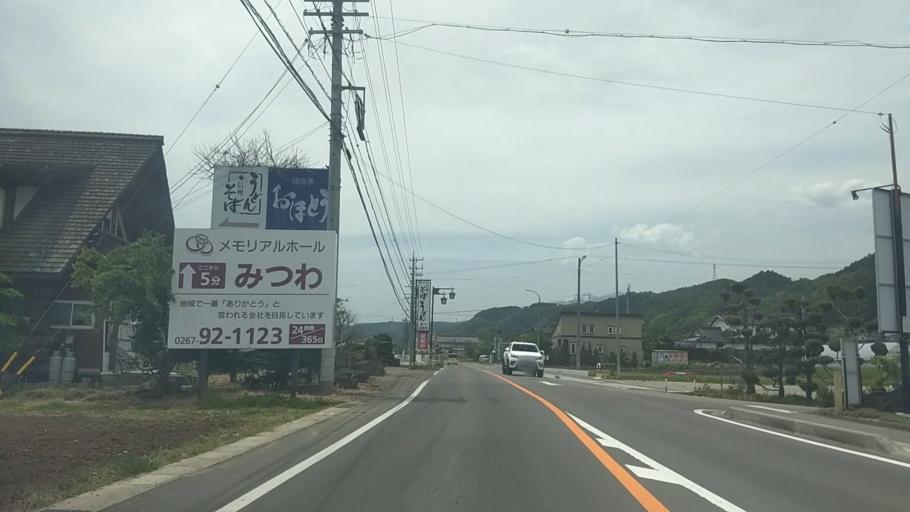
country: JP
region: Nagano
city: Saku
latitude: 36.1494
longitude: 138.4748
